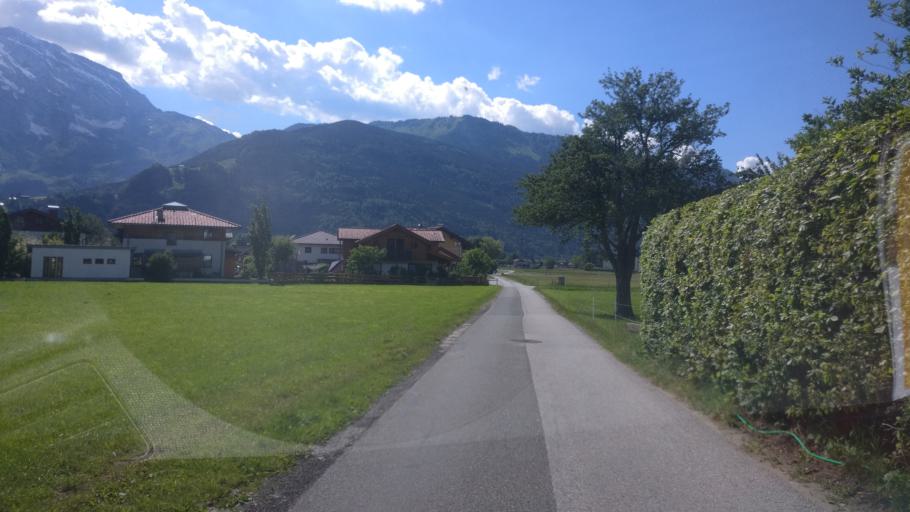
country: AT
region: Salzburg
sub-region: Politischer Bezirk Hallein
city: Golling an der Salzach
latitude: 47.6183
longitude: 13.1640
